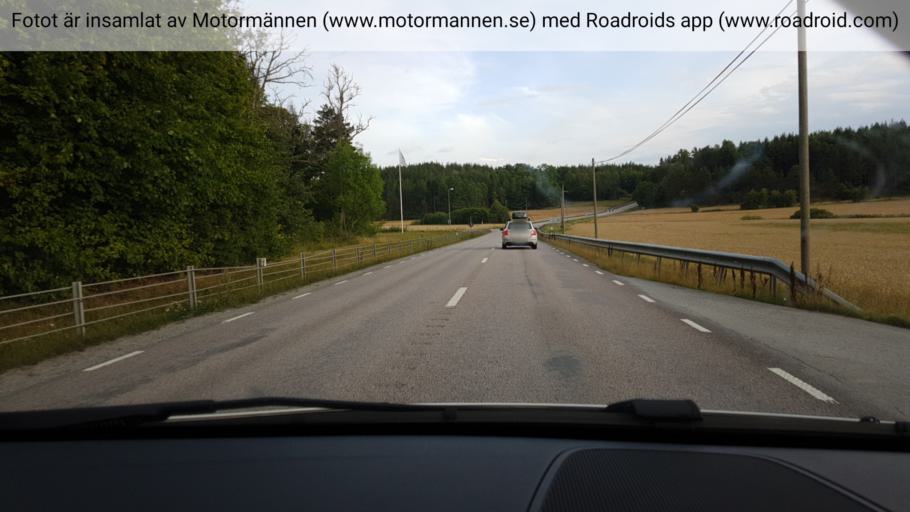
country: SE
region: Stockholm
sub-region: Sigtuna Kommun
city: Sigtuna
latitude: 59.6499
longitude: 17.7012
